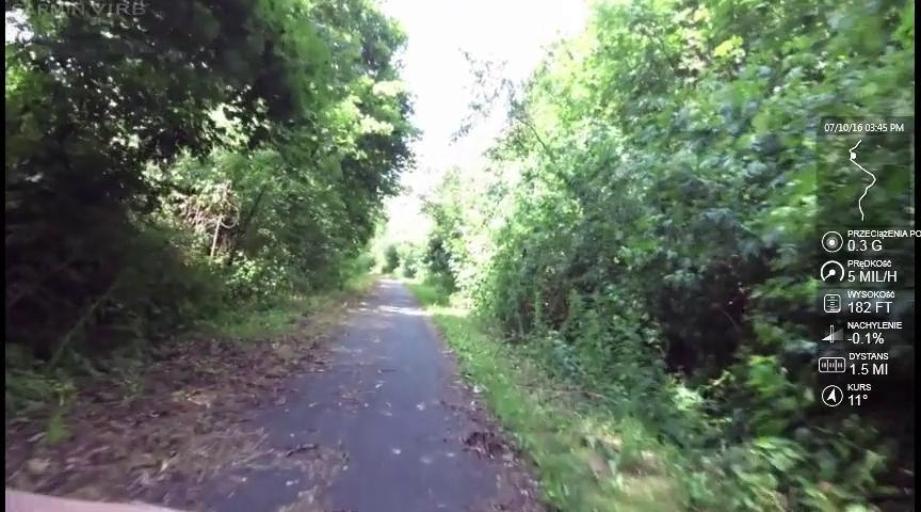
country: PL
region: West Pomeranian Voivodeship
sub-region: Powiat gryfinski
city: Banie
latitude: 53.1316
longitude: 14.6182
